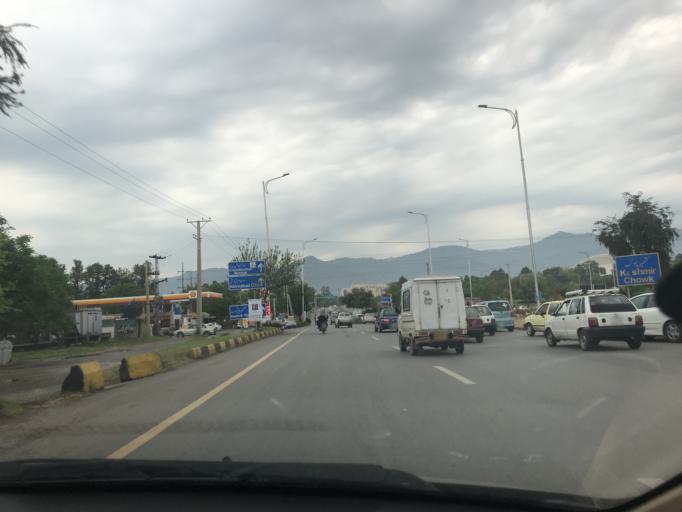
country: PK
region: Islamabad
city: Islamabad
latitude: 33.7079
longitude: 73.1056
